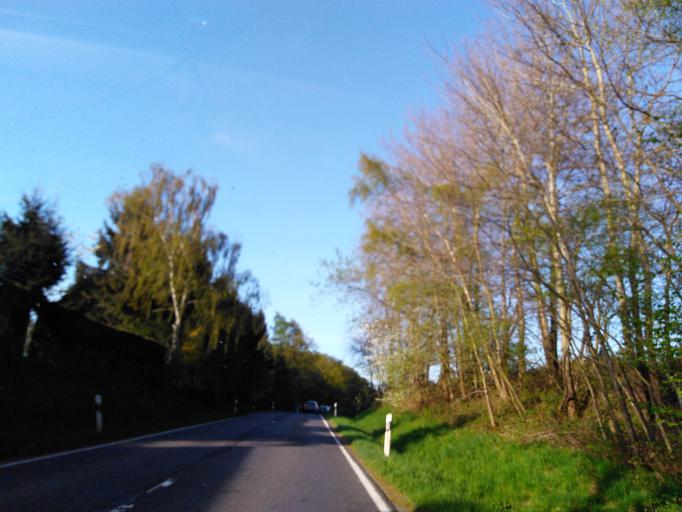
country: DE
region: North Rhine-Westphalia
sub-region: Regierungsbezirk Koln
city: Hennef
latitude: 50.8536
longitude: 7.3004
